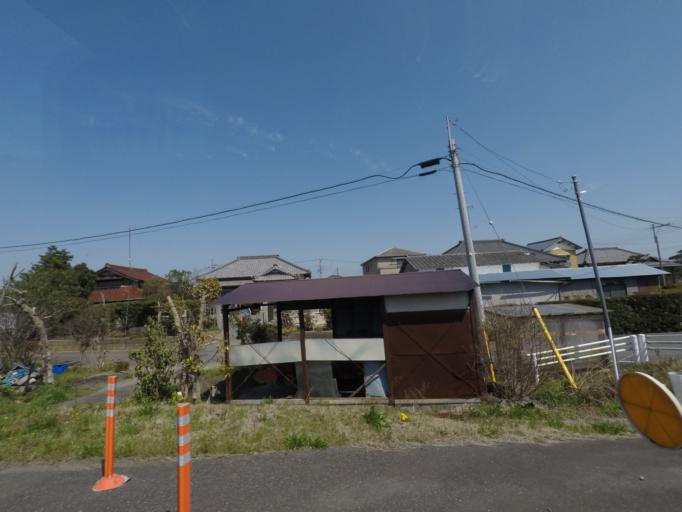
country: JP
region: Ibaraki
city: Edosaki
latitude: 35.8672
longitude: 140.3090
